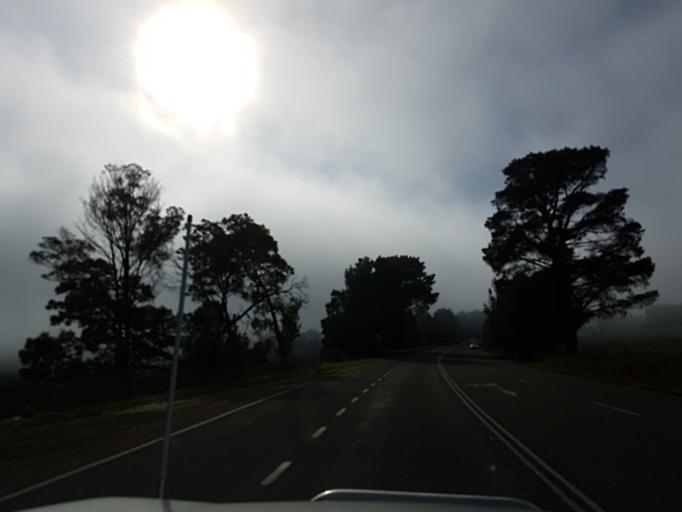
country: AU
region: Victoria
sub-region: Murrindindi
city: Kinglake West
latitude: -37.4233
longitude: 145.4230
